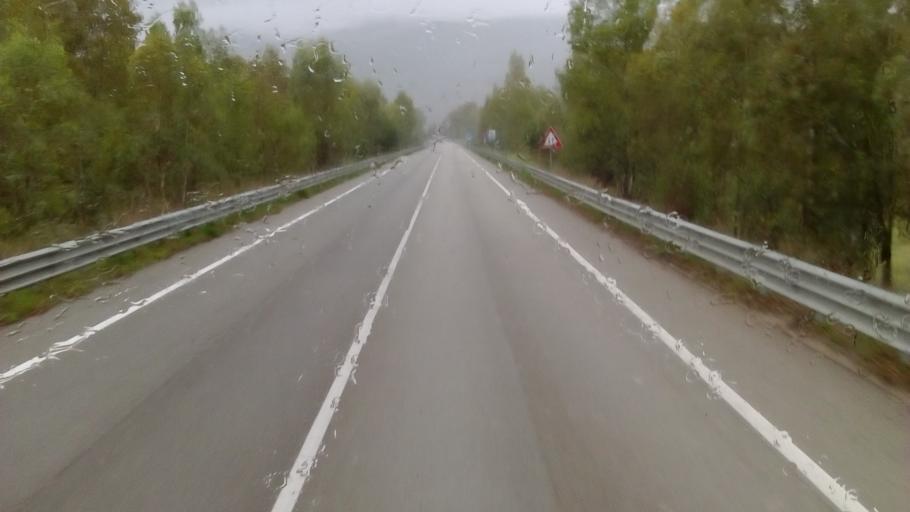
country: IT
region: Sicily
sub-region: Enna
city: Villarosa
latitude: 37.5292
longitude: 14.1290
